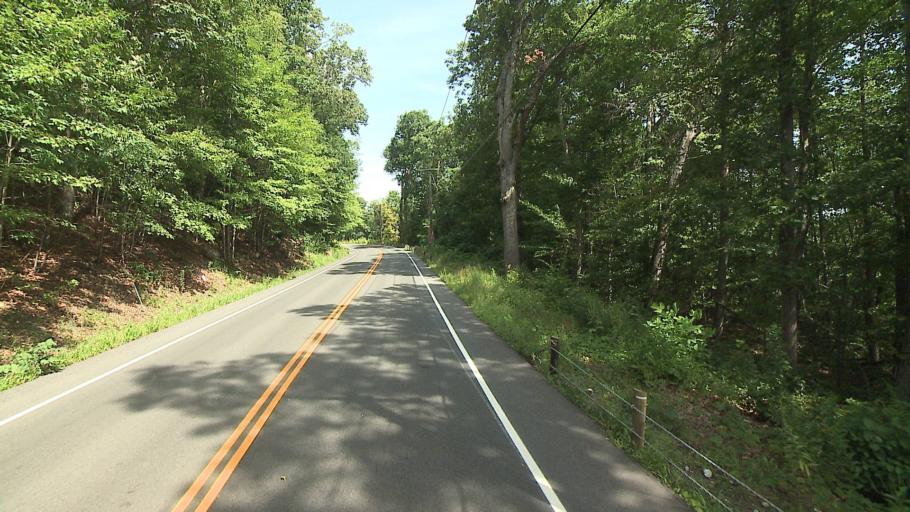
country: US
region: Connecticut
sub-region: Litchfield County
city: Bethlehem Village
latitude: 41.6086
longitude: -73.1782
